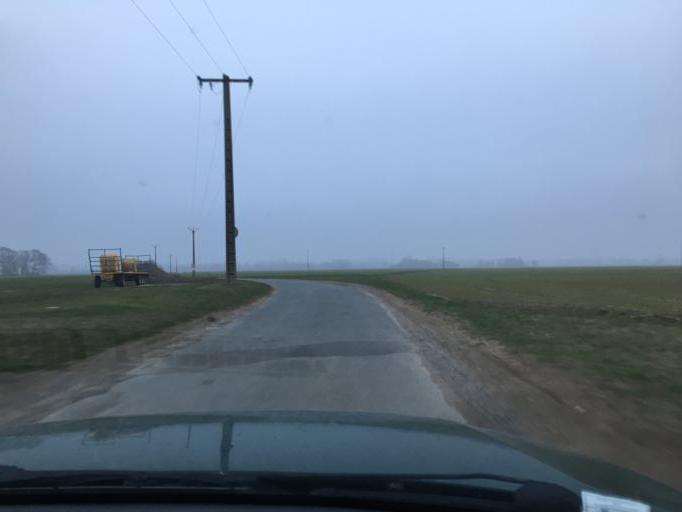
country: FR
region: Centre
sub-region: Departement du Loiret
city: Beaugency
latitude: 47.7703
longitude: 1.6458
